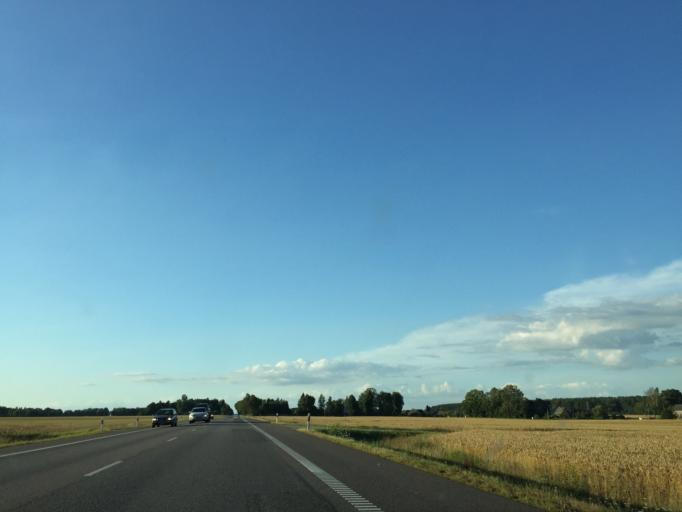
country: LT
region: Panevezys
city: Pasvalys
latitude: 55.9540
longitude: 24.3387
